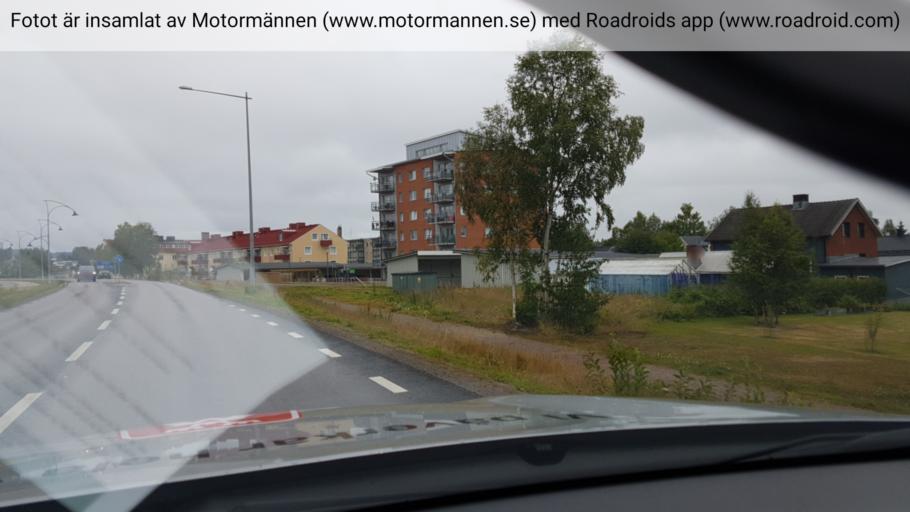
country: SE
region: Norrbotten
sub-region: Gallivare Kommun
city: Gaellivare
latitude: 67.1308
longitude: 20.6717
